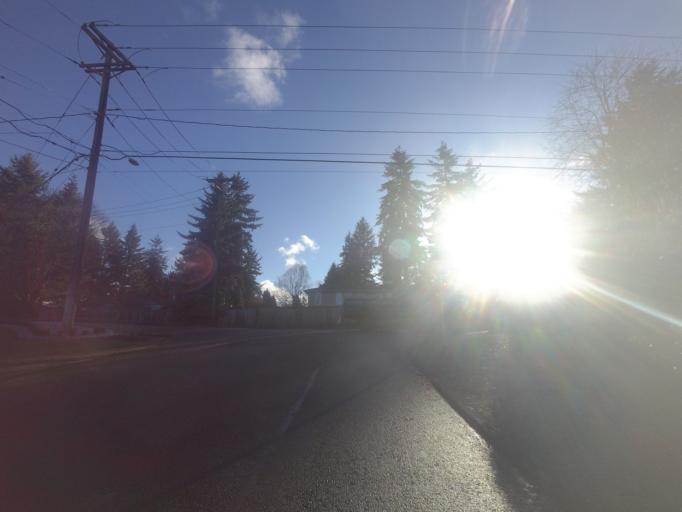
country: US
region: Washington
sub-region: Pierce County
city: Fircrest
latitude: 47.2248
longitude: -122.5251
